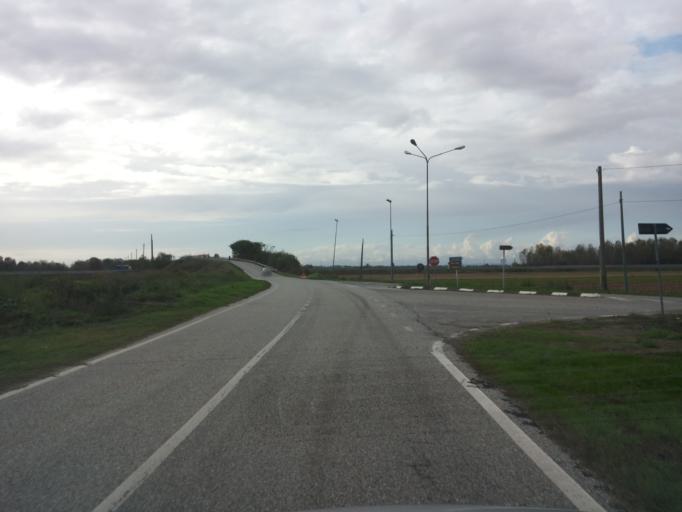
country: IT
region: Piedmont
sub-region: Provincia di Vercelli
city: Pezzana
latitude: 45.2595
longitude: 8.4718
